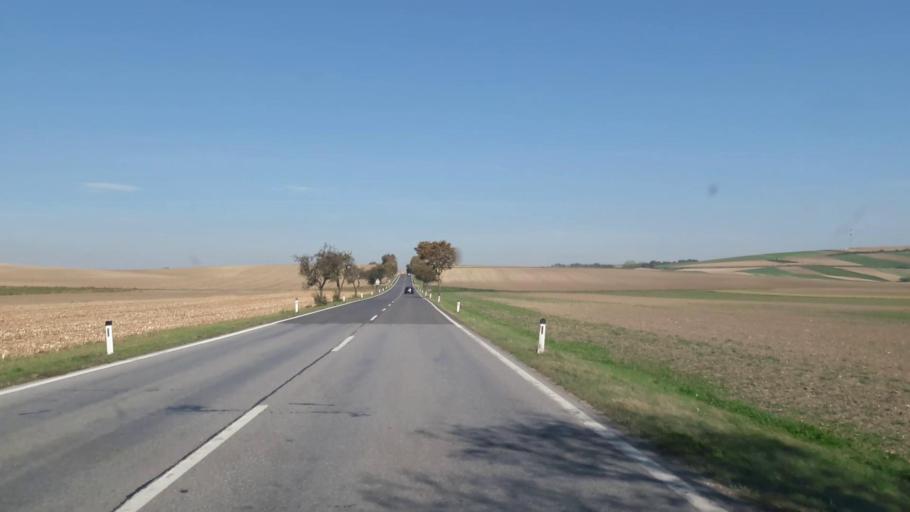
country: AT
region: Lower Austria
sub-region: Politischer Bezirk Korneuburg
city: Harmannsdorf
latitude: 48.4140
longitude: 16.3808
